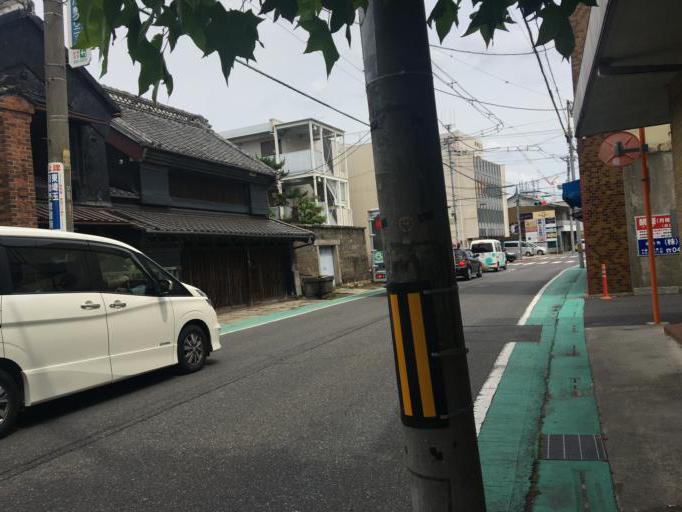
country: JP
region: Saitama
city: Koshigaya
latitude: 35.8936
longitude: 139.7862
